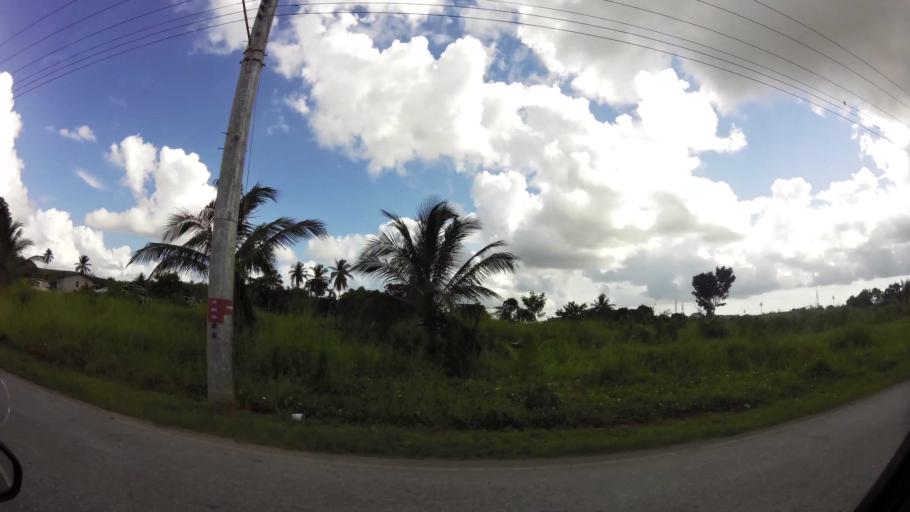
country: TT
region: Penal/Debe
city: Debe
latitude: 10.2250
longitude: -61.4385
